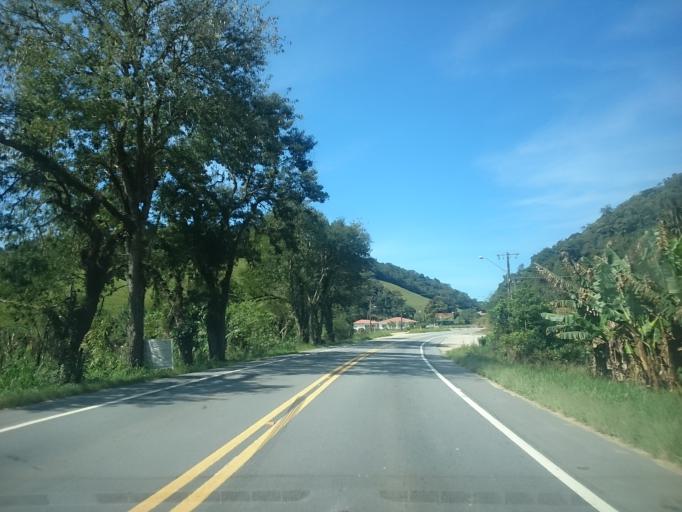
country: BR
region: Santa Catarina
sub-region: Santo Amaro Da Imperatriz
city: Santo Amaro da Imperatriz
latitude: -27.7151
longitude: -48.8760
